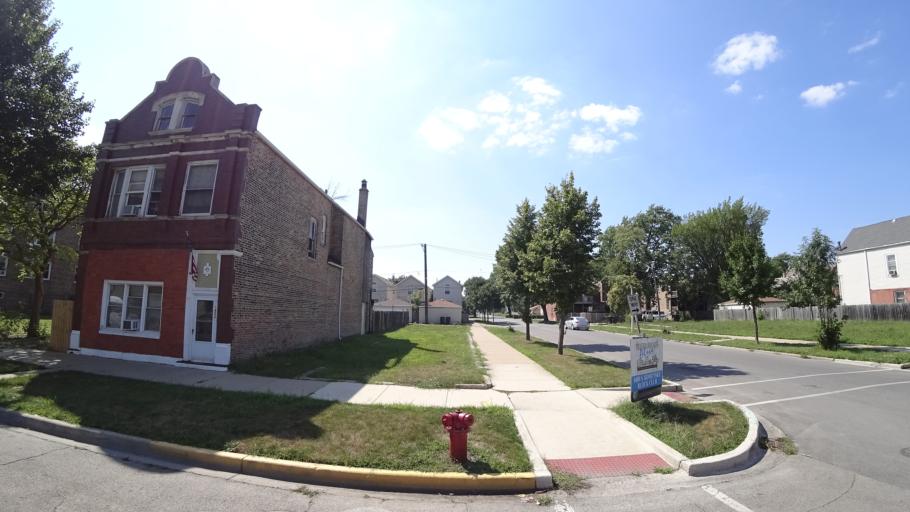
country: US
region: Illinois
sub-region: Cook County
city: Cicero
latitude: 41.8624
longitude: -87.7263
